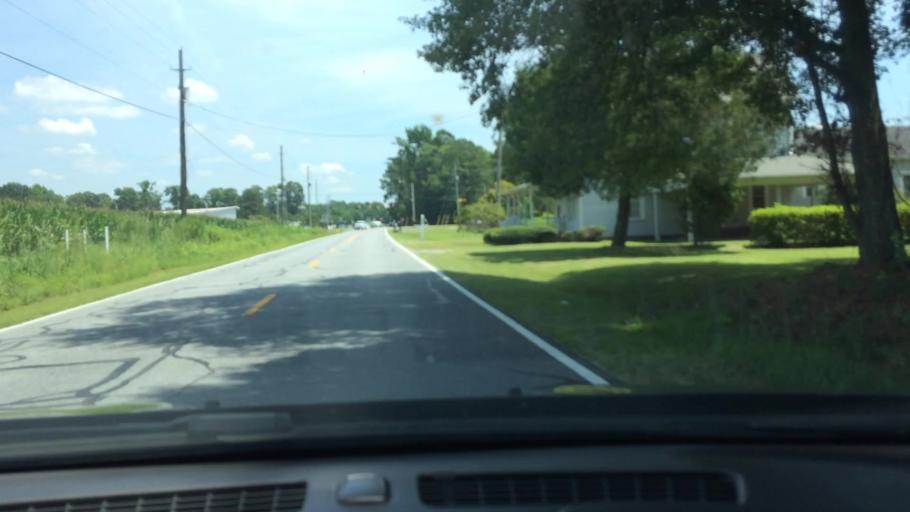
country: US
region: North Carolina
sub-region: Pitt County
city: Windsor
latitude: 35.5112
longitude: -77.3204
